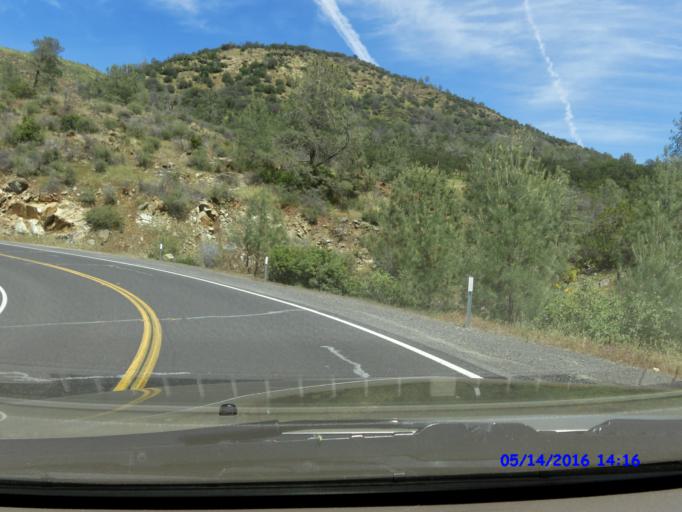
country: US
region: California
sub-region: Mariposa County
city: Mariposa
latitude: 37.6569
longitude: -120.1464
